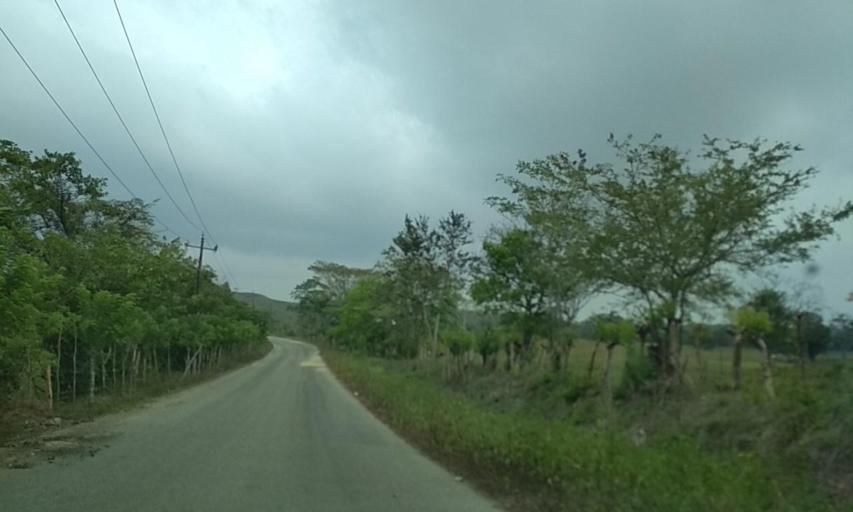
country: MX
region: Tabasco
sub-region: Huimanguillo
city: Francisco Rueda
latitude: 17.6047
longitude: -94.0932
